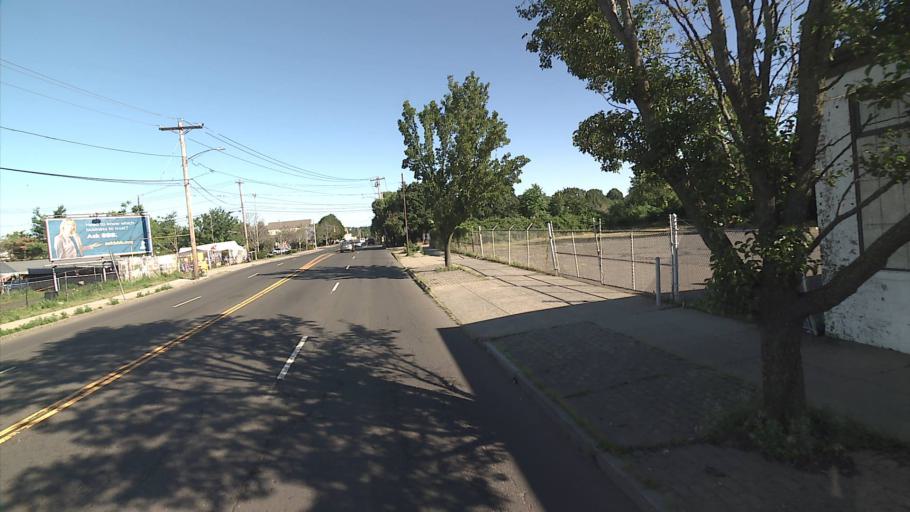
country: US
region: Connecticut
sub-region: New Haven County
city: New Haven
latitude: 41.2935
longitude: -72.9444
